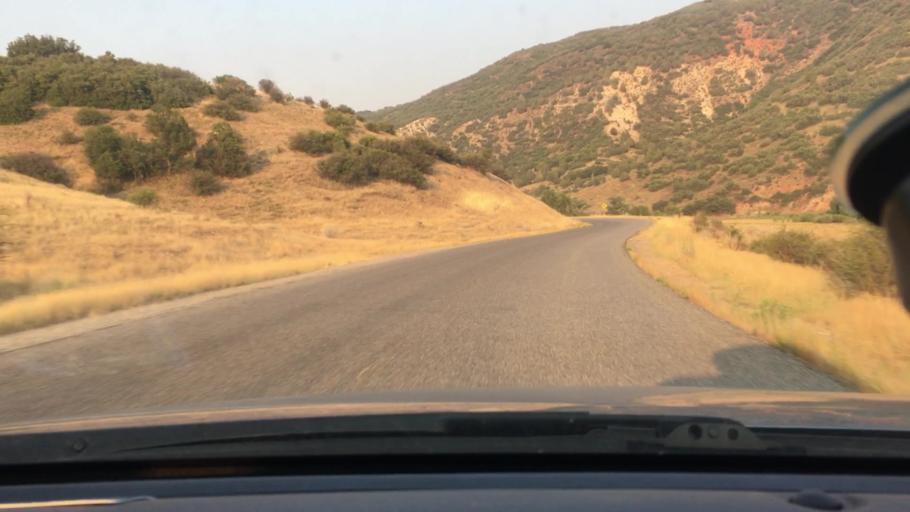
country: US
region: Utah
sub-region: Utah County
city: Mapleton
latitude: 40.0472
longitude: -111.4721
